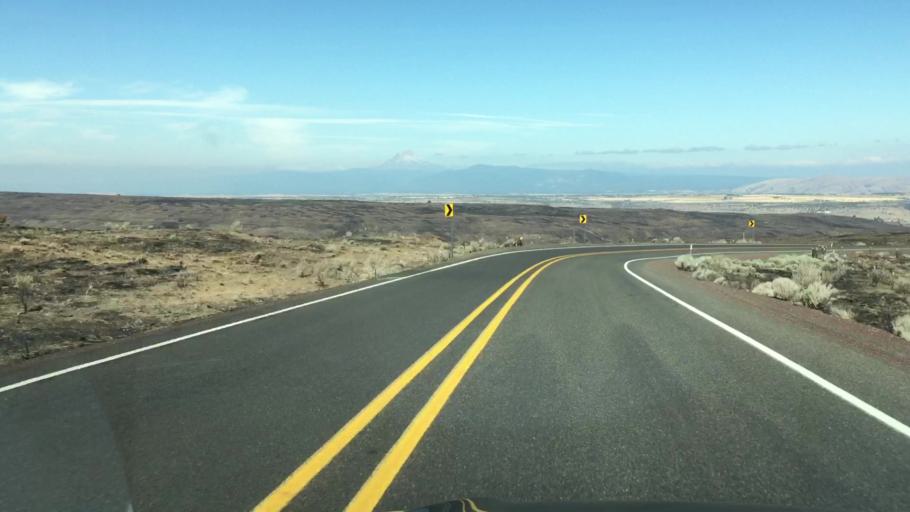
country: US
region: Oregon
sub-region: Jefferson County
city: Warm Springs
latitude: 45.1192
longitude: -121.0463
